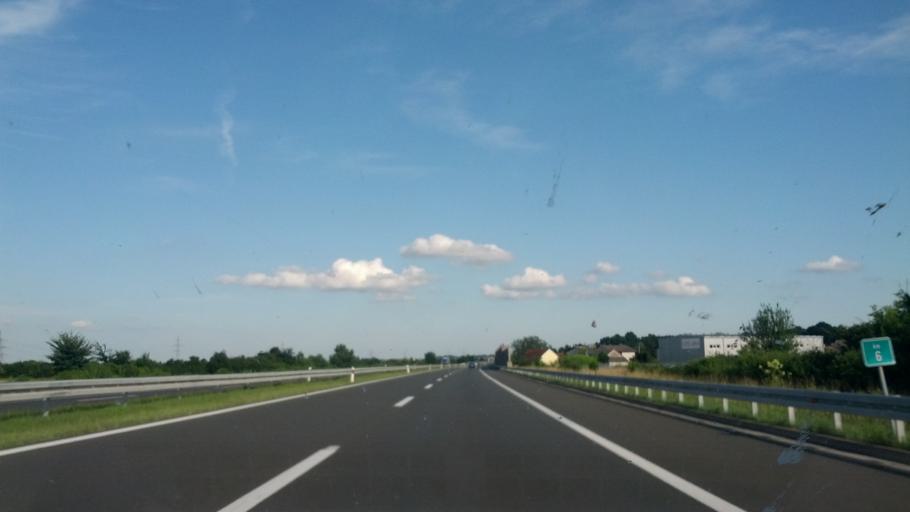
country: HR
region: Zagrebacka
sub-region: Grad Samobor
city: Samobor
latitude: 45.8159
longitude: 15.7590
